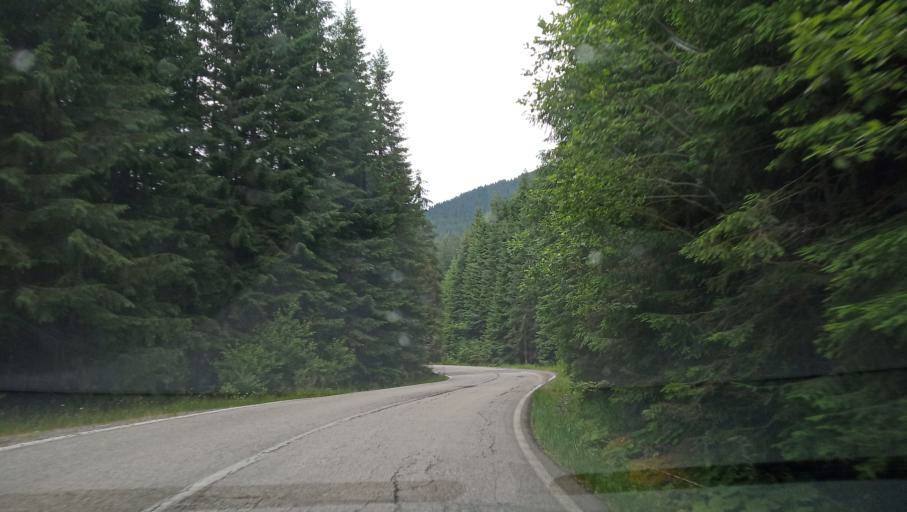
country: RO
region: Valcea
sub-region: Comuna Voineasa
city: Voineasa
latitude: 45.4228
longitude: 23.7603
